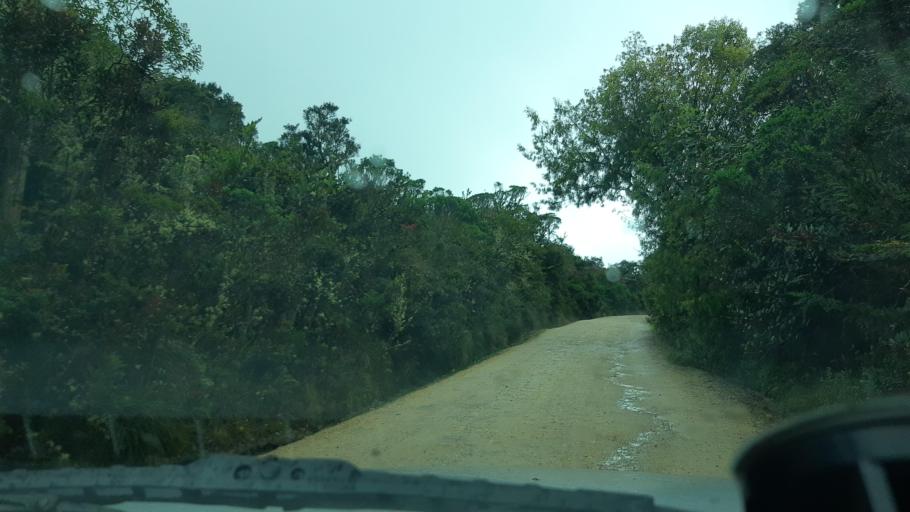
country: CO
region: Cundinamarca
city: Villapinzon
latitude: 5.2080
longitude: -73.5579
